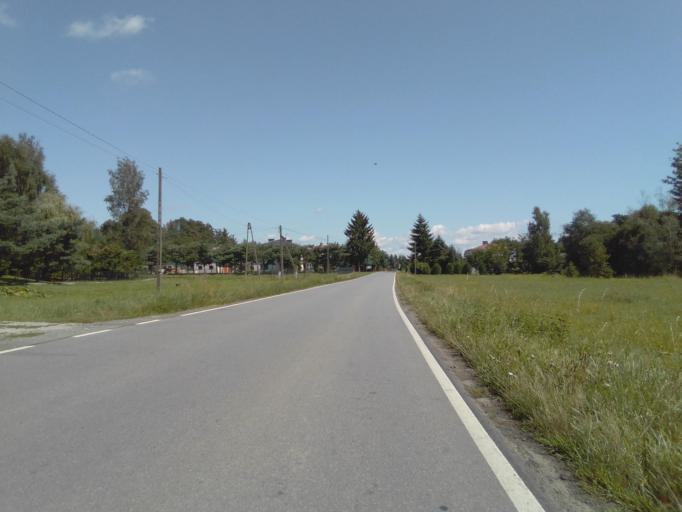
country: PL
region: Subcarpathian Voivodeship
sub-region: Powiat krosnienski
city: Jedlicze
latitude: 49.6969
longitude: 21.6175
